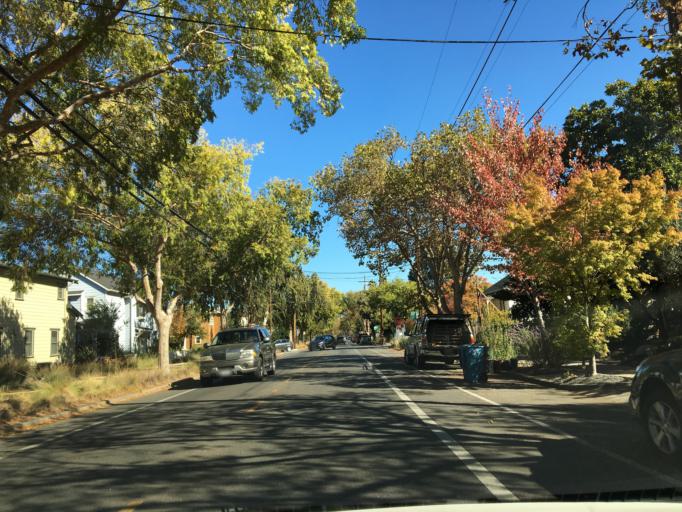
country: US
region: California
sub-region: Santa Clara County
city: Stanford
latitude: 37.4256
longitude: -122.1510
